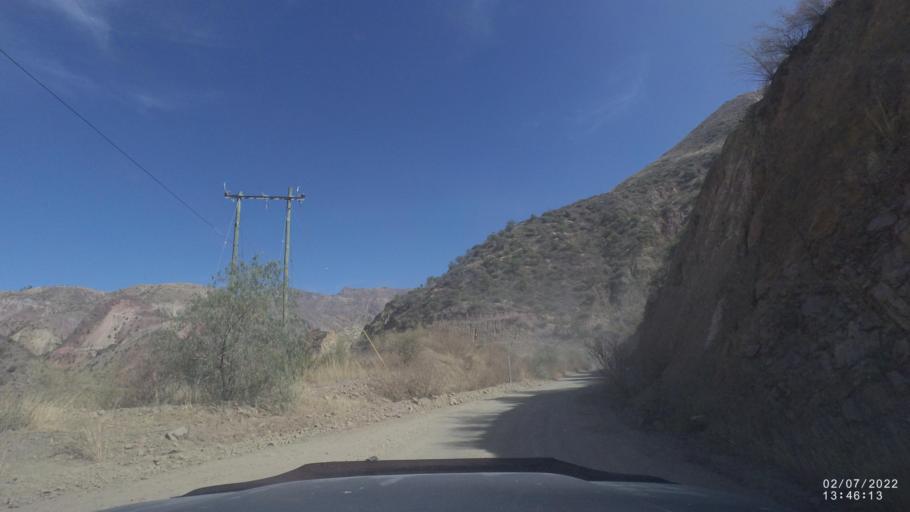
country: BO
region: Cochabamba
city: Irpa Irpa
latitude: -17.8127
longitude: -66.3659
